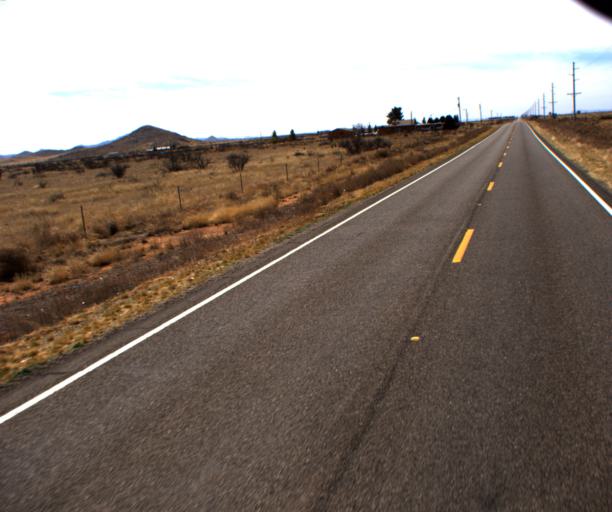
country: US
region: Arizona
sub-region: Cochise County
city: Willcox
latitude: 31.8747
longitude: -109.6952
